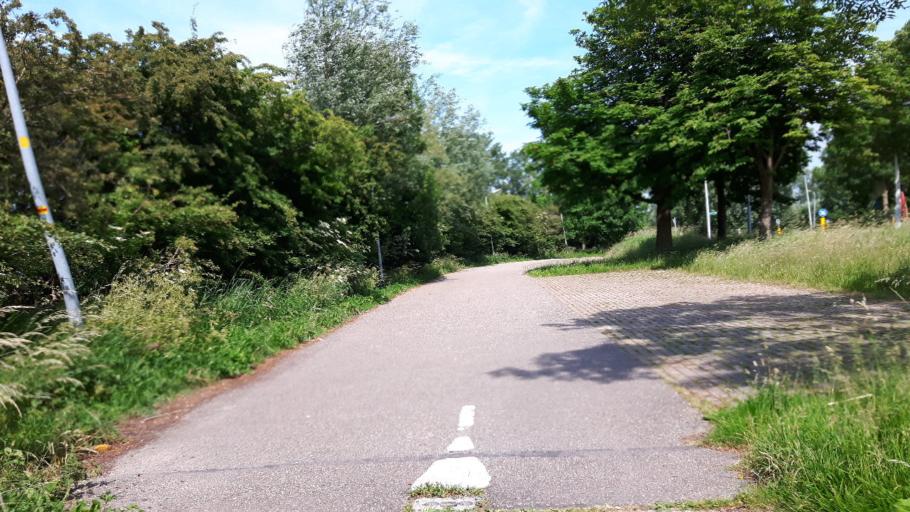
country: NL
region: North Holland
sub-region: Gemeente Uithoorn
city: Uithoorn
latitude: 52.2275
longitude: 4.8116
